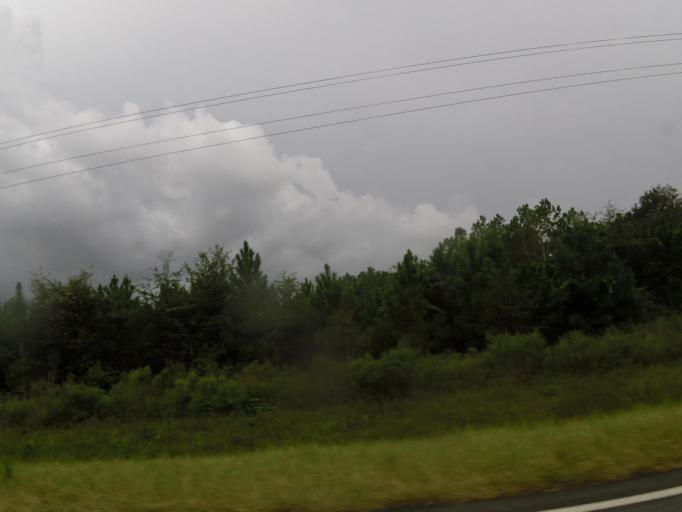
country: US
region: Florida
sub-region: Baker County
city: Macclenny
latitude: 30.3822
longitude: -82.1689
